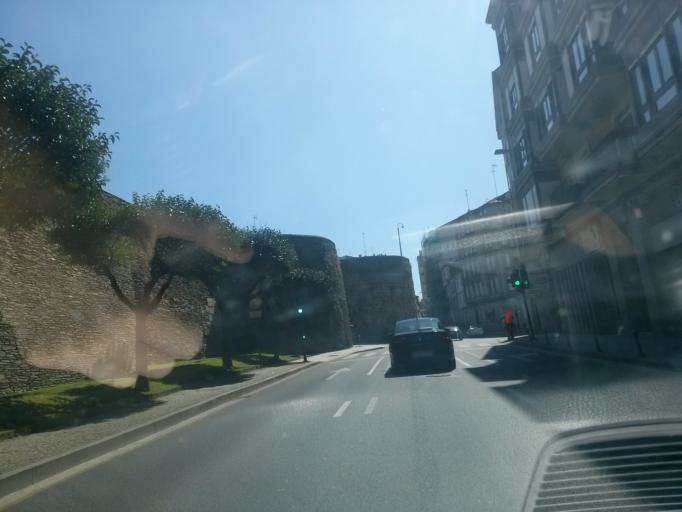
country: ES
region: Galicia
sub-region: Provincia de Lugo
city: Lugo
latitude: 43.0093
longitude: -7.5598
